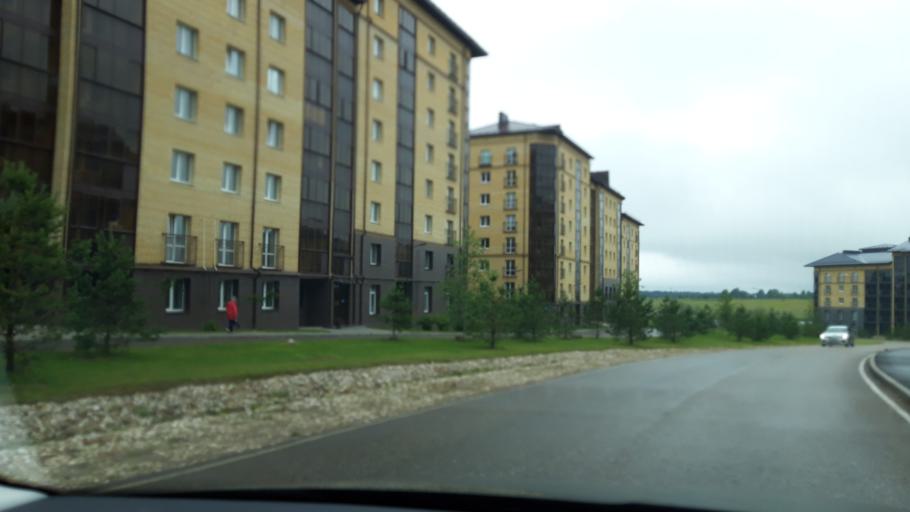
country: RU
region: Tverskaya
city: Zavidovo
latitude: 56.5790
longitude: 36.5200
